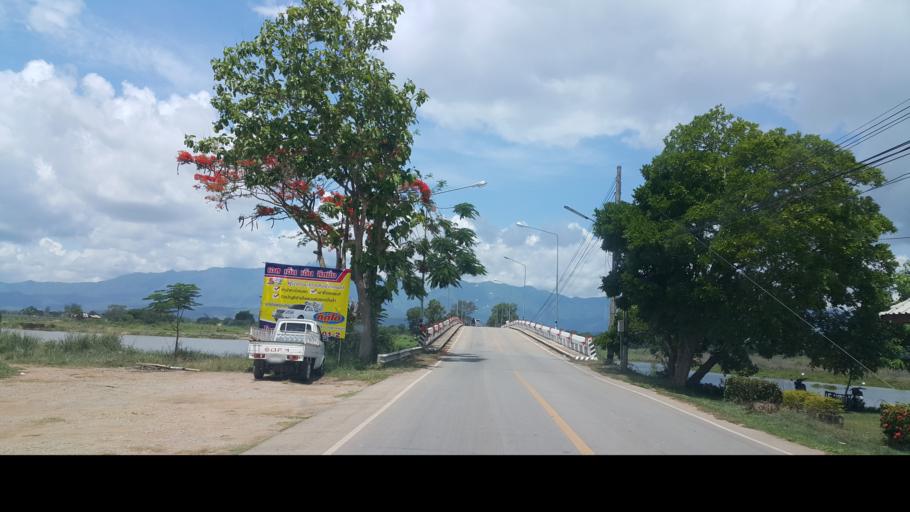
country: TH
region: Phayao
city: Phayao
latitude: 19.2039
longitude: 99.8686
